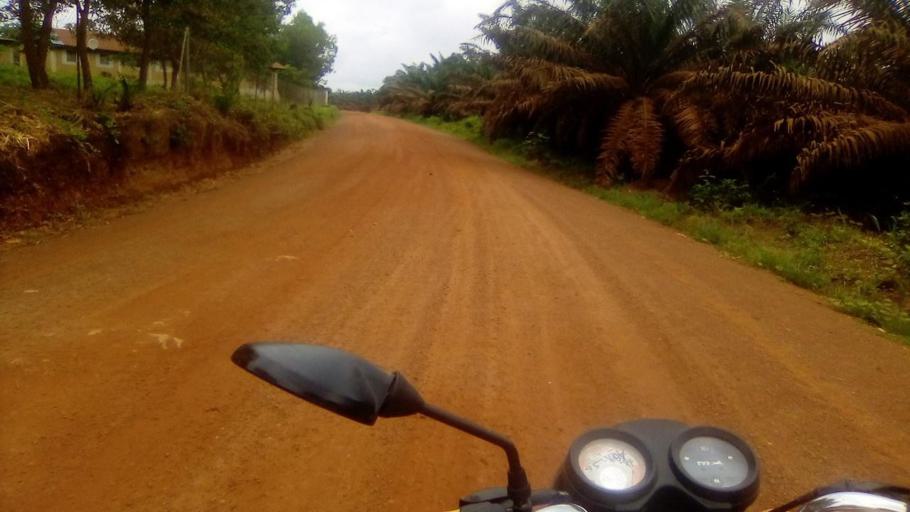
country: SL
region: Southern Province
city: Tongole
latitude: 7.4343
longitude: -11.8588
